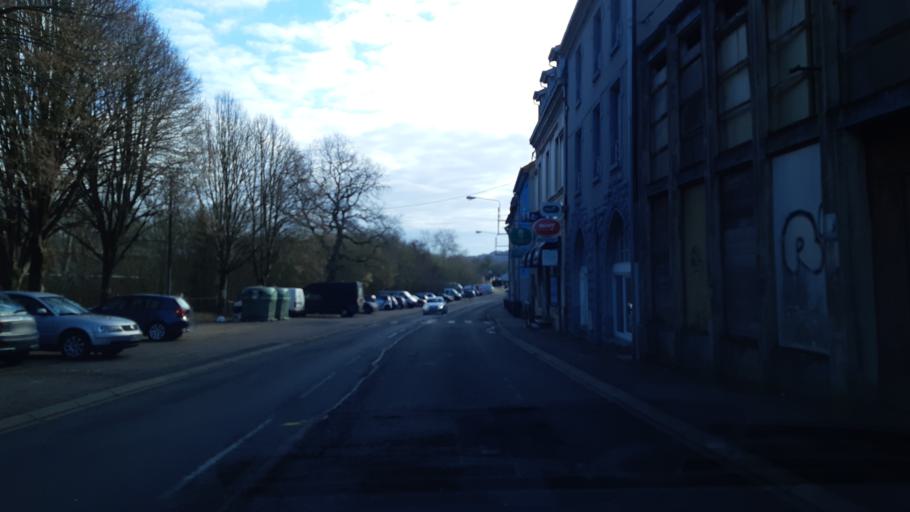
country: FR
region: Lorraine
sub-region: Departement de Meurthe-et-Moselle
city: Villerupt
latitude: 49.4744
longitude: 5.9374
